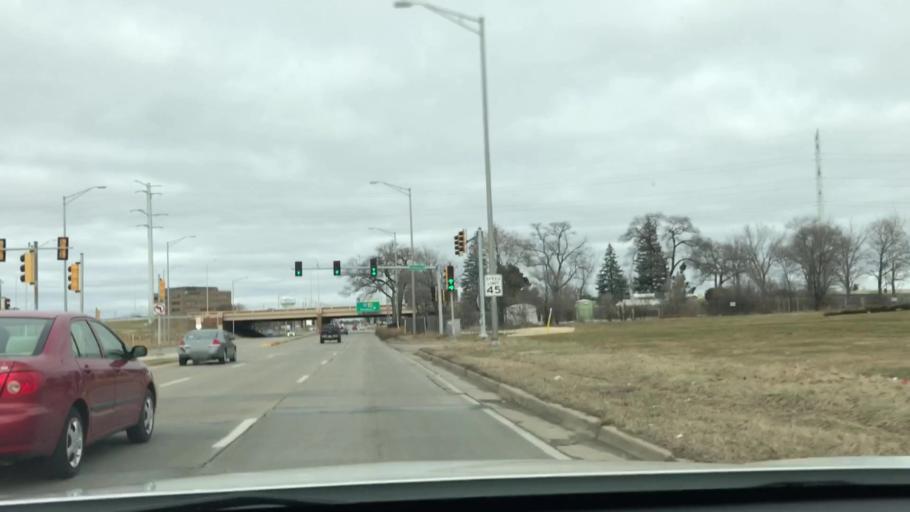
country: US
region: Illinois
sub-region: Cook County
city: Elk Grove Village
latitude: 42.0384
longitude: -87.9840
